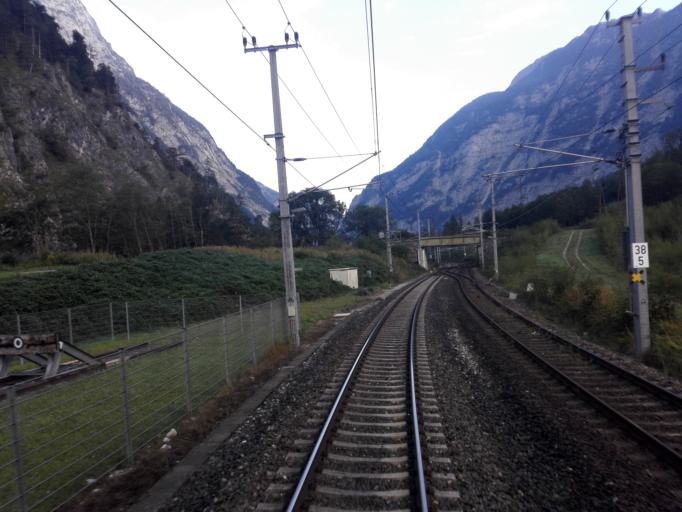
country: AT
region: Salzburg
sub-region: Politischer Bezirk Sankt Johann im Pongau
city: Werfen
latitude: 47.5255
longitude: 13.1661
